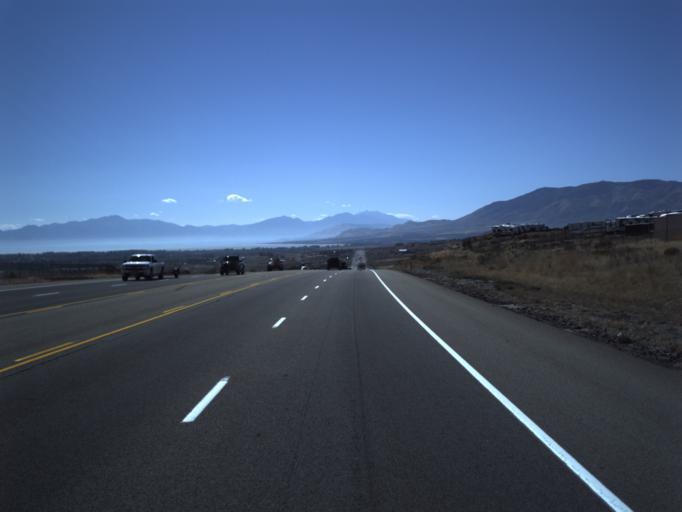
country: US
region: Utah
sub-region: Salt Lake County
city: Bluffdale
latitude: 40.4316
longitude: -111.9286
